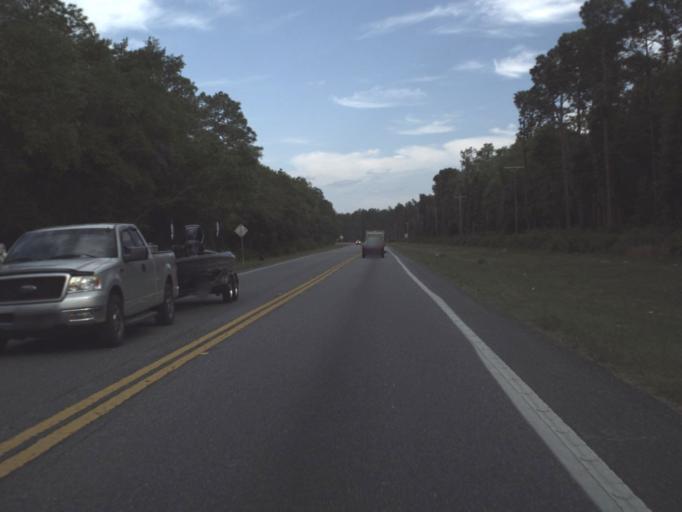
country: US
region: Florida
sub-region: Marion County
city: Silver Springs Shores
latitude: 29.1919
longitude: -81.9099
